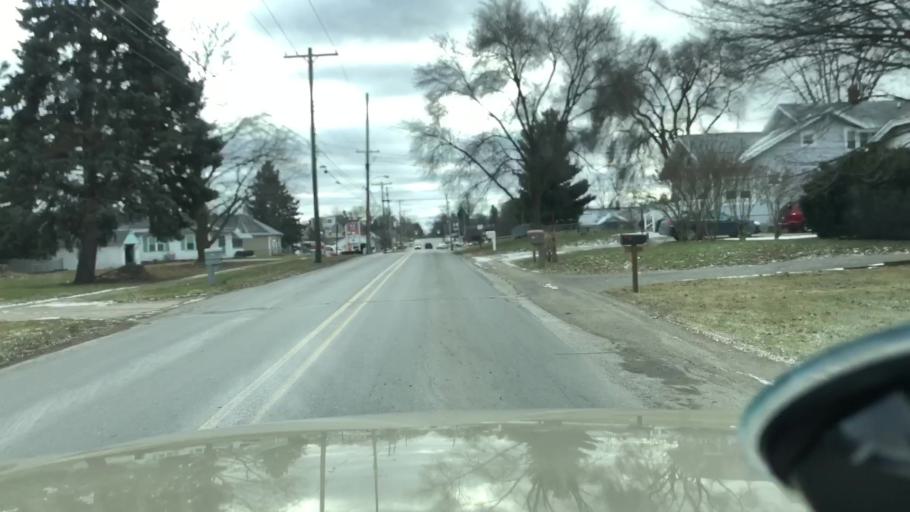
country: US
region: Michigan
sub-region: Jackson County
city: Jackson
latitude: 42.2585
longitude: -84.3650
